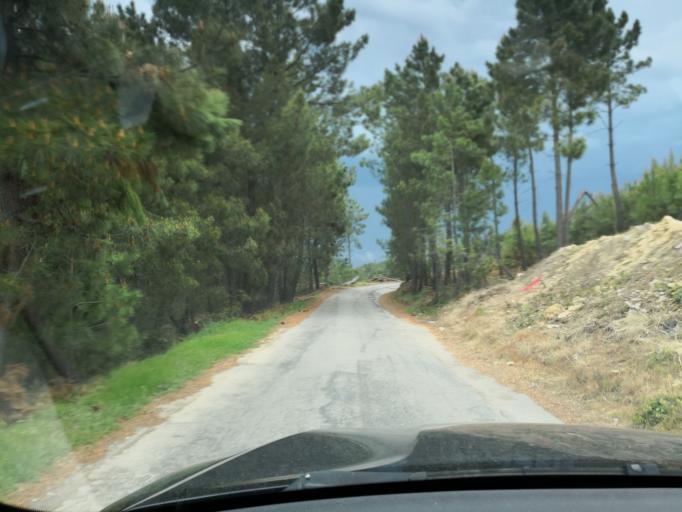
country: PT
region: Vila Real
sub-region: Sabrosa
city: Vilela
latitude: 41.2461
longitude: -7.6610
